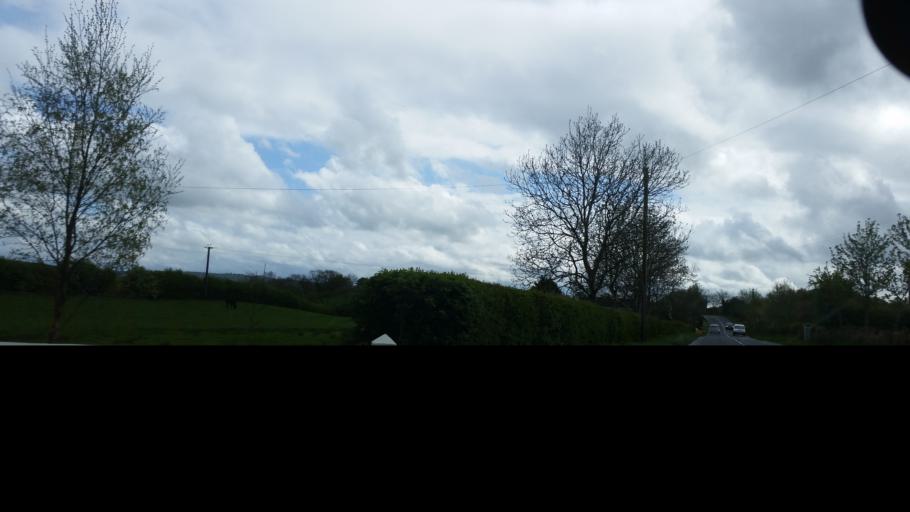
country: GB
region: Northern Ireland
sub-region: Omagh District
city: Omagh
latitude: 54.5479
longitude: -7.2865
